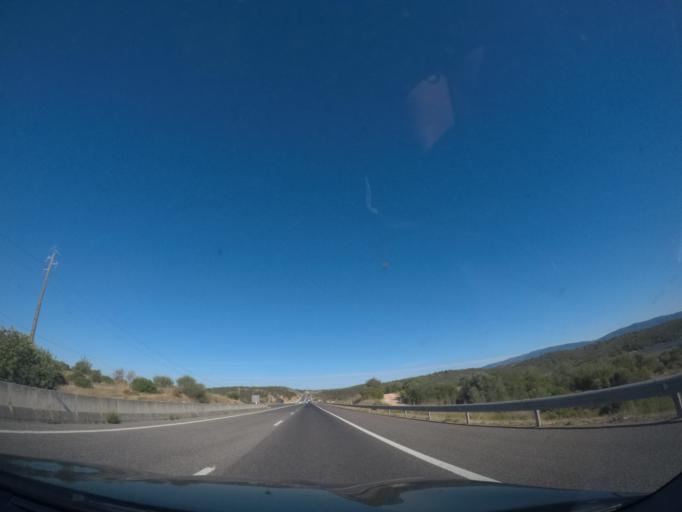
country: PT
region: Faro
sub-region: Lagoa
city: Estombar
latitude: 37.1600
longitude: -8.4976
